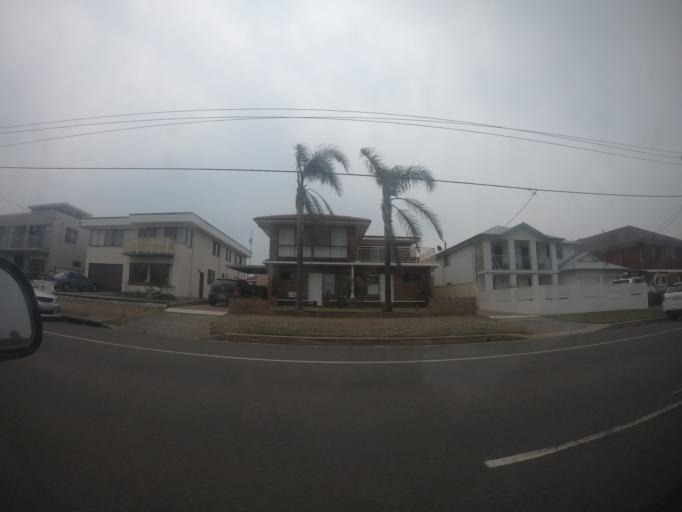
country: AU
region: New South Wales
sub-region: Shellharbour
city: Lake Illawarra
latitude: -34.5483
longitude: 150.8691
